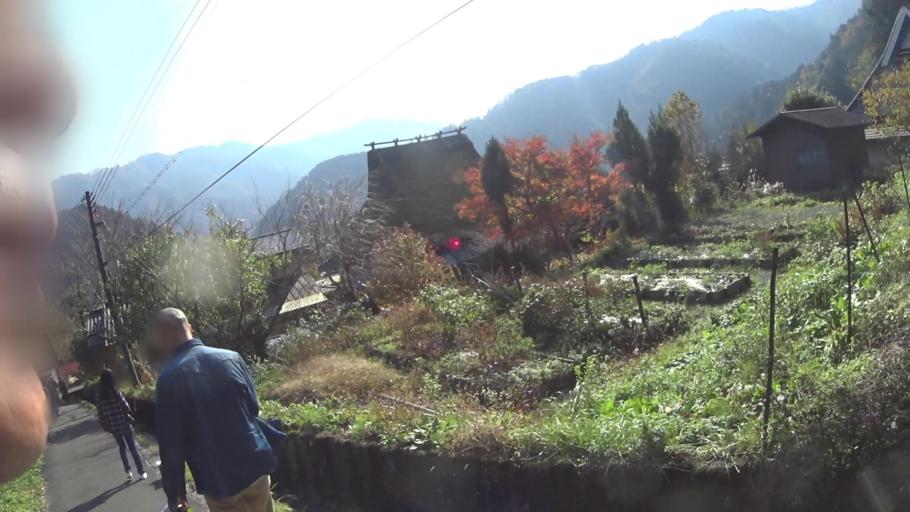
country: JP
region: Fukui
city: Obama
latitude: 35.3144
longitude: 135.6232
